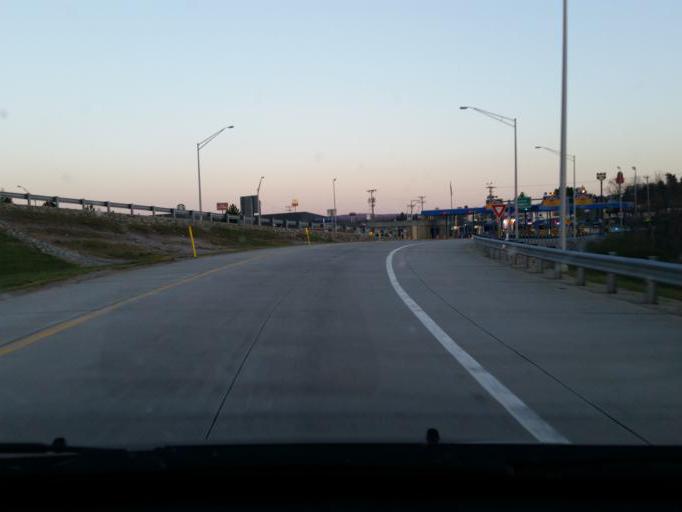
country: US
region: Pennsylvania
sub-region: Somerset County
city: Somerset
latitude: 40.0205
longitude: -79.0827
